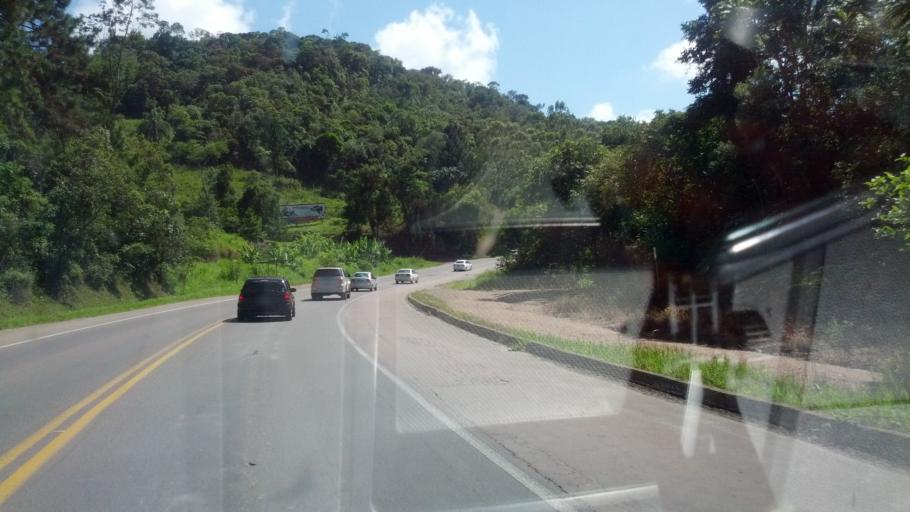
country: BR
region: Santa Catarina
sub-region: Ibirama
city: Ibirama
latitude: -27.1482
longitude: -49.5560
